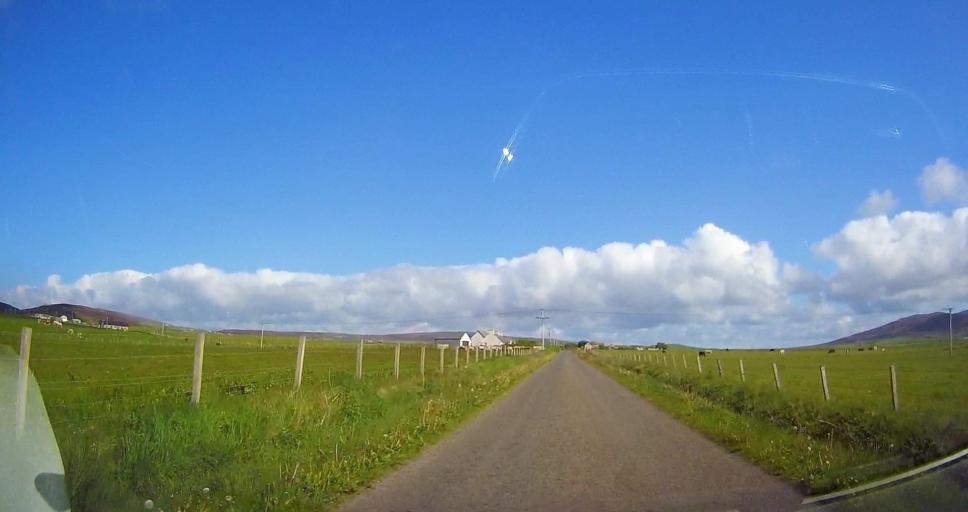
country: GB
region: Scotland
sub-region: Orkney Islands
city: Stromness
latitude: 58.9977
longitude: -3.1662
